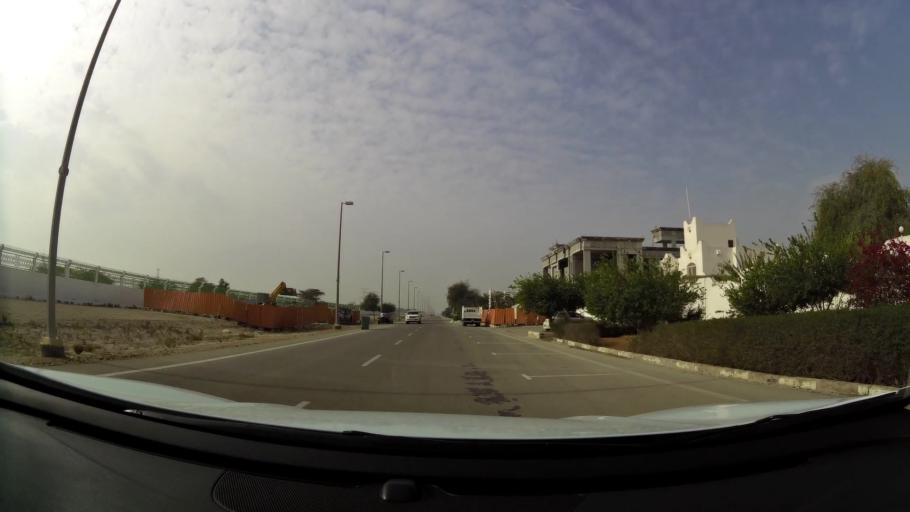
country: AE
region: Abu Dhabi
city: Abu Dhabi
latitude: 24.6635
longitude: 54.7719
